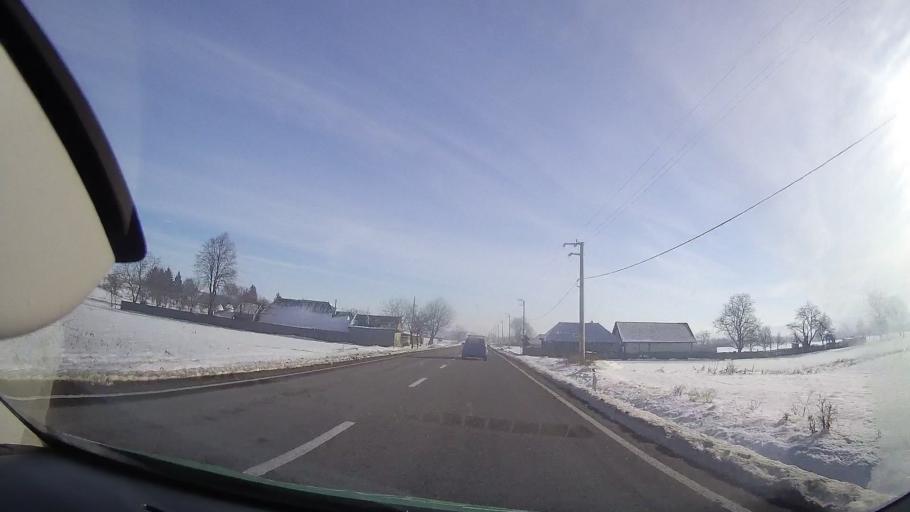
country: RO
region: Neamt
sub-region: Comuna Ghindaoani
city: Ghindaoani
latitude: 47.0805
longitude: 26.3450
